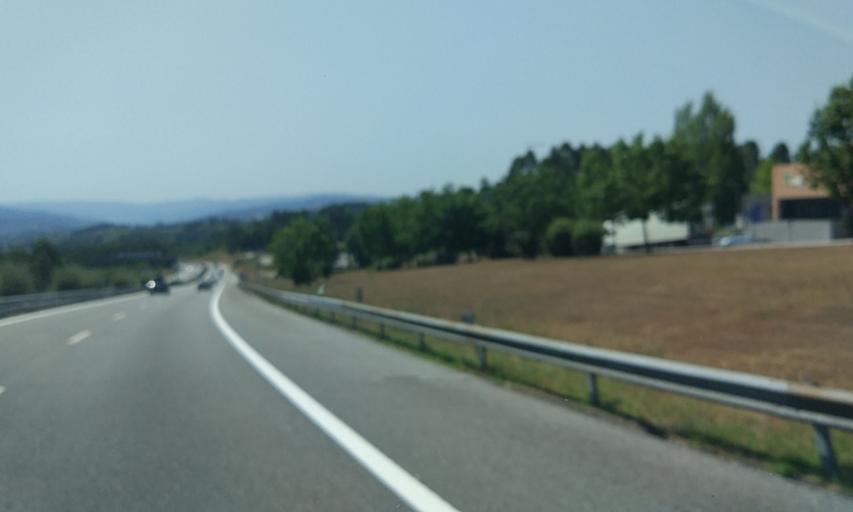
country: PT
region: Porto
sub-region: Amarante
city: Figueiro
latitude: 41.2382
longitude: -8.1896
